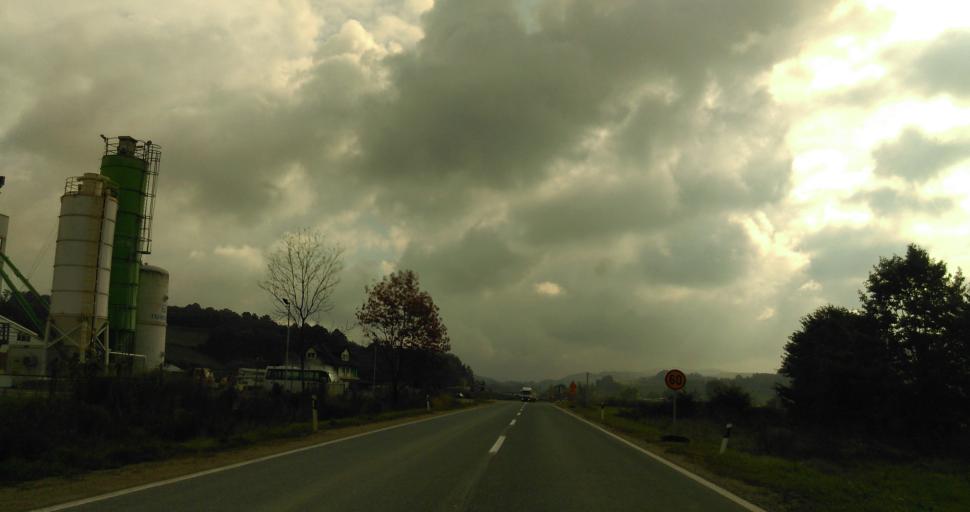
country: RS
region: Central Serbia
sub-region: Kolubarski Okrug
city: Ljig
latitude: 44.2003
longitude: 20.2652
